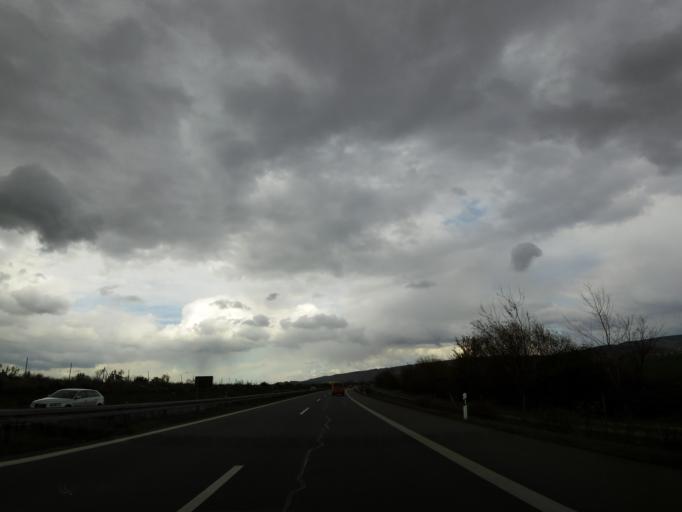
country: DE
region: Saxony-Anhalt
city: Wernigerode
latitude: 51.8677
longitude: 10.7905
